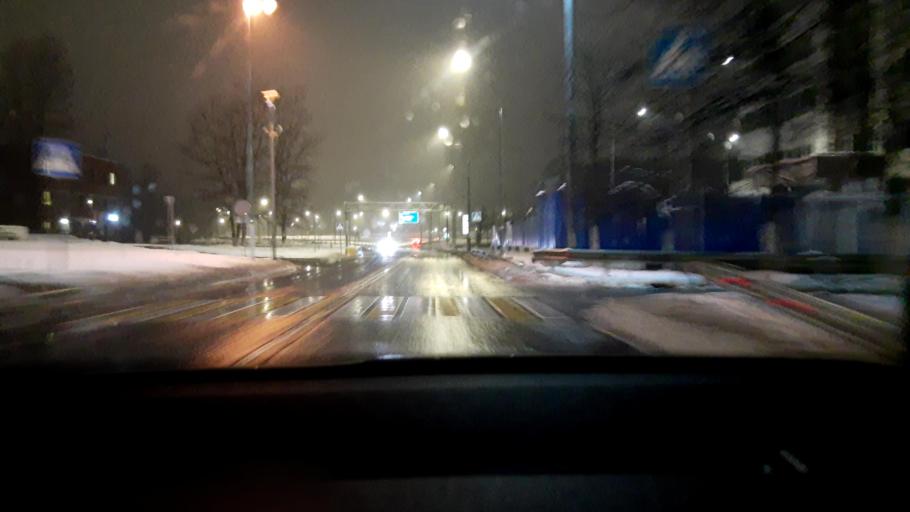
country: RU
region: Moskovskaya
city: Vostryakovo
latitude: 55.4305
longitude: 37.8742
